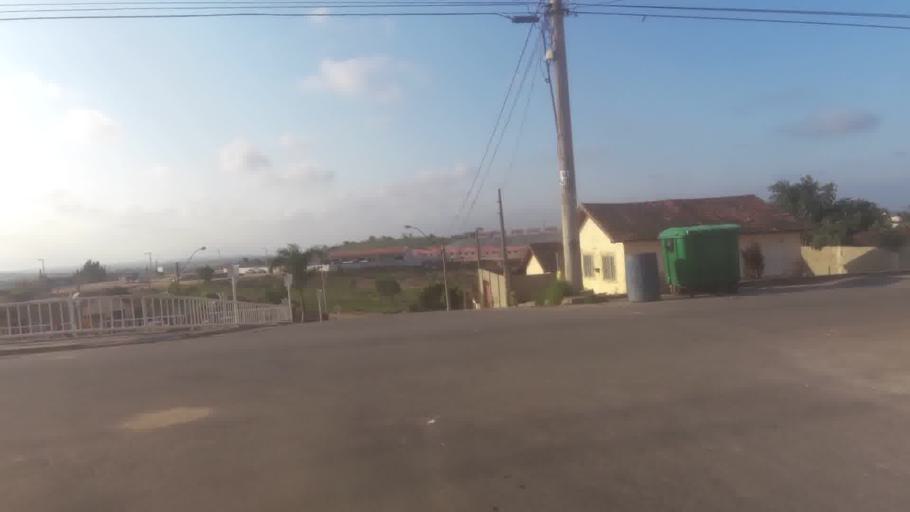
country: BR
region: Espirito Santo
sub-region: Itapemirim
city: Itapemirim
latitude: -21.0190
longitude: -40.8349
